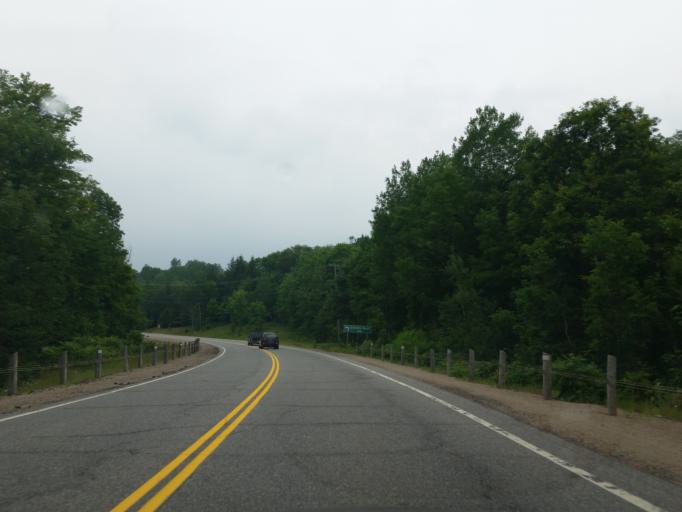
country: CA
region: Ontario
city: Huntsville
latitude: 45.3658
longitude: -79.1072
